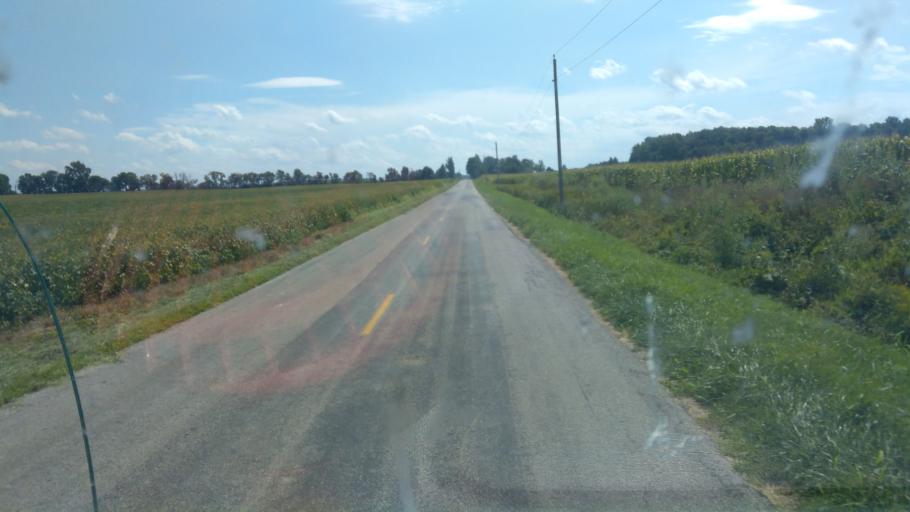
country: US
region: Ohio
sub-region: Wyandot County
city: Upper Sandusky
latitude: 40.6422
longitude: -83.3430
